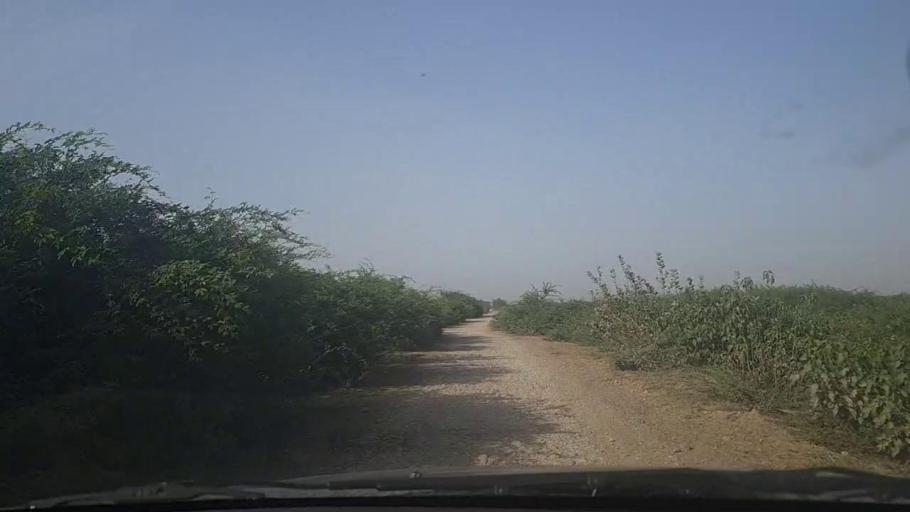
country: PK
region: Sindh
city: Keti Bandar
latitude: 24.2550
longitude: 67.5627
